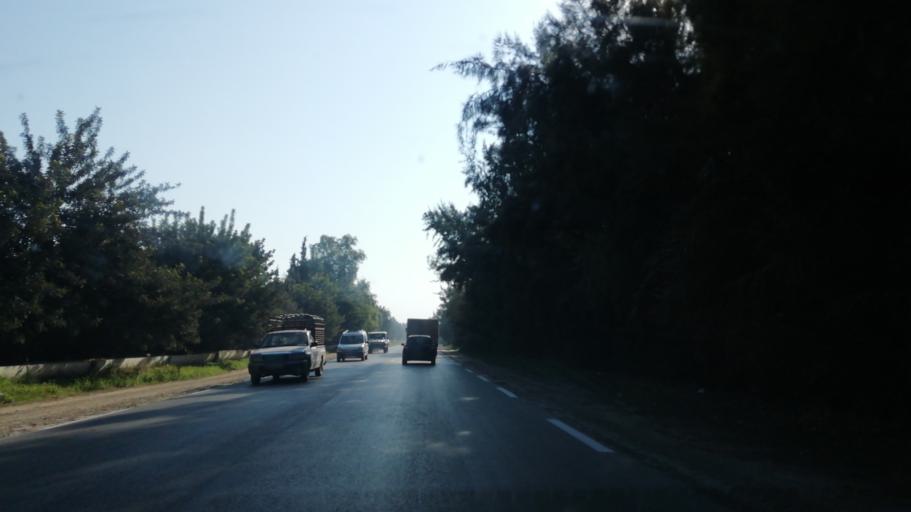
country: DZ
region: Relizane
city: Relizane
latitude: 35.7284
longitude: 0.4762
